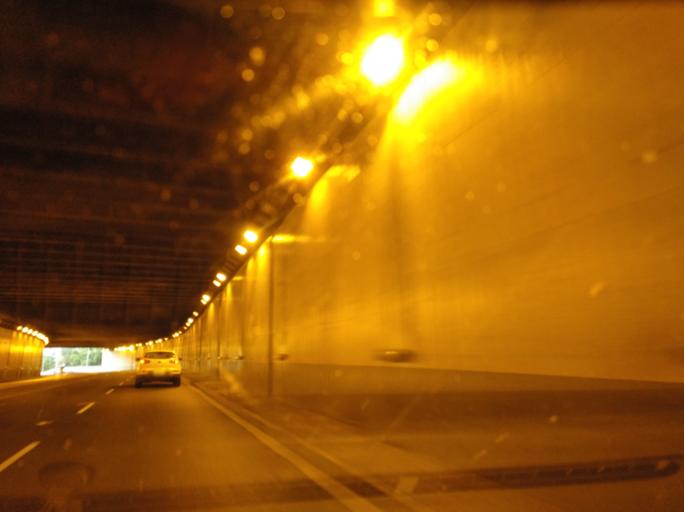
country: ES
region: Catalonia
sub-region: Provincia de Barcelona
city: Horta-Guinardo
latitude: 41.4277
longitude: 2.1576
